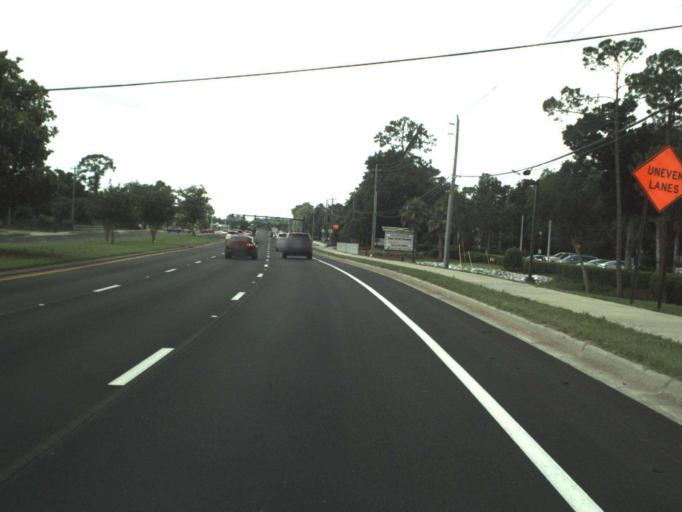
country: US
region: Florida
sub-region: Volusia County
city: Port Orange
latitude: 29.1148
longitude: -81.0247
